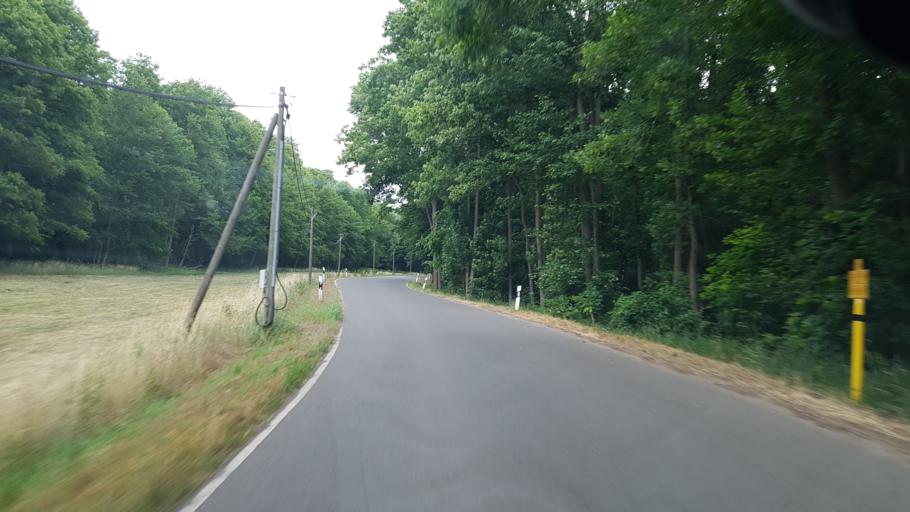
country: DE
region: Brandenburg
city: Kasel-Golzig
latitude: 51.9539
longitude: 13.6543
